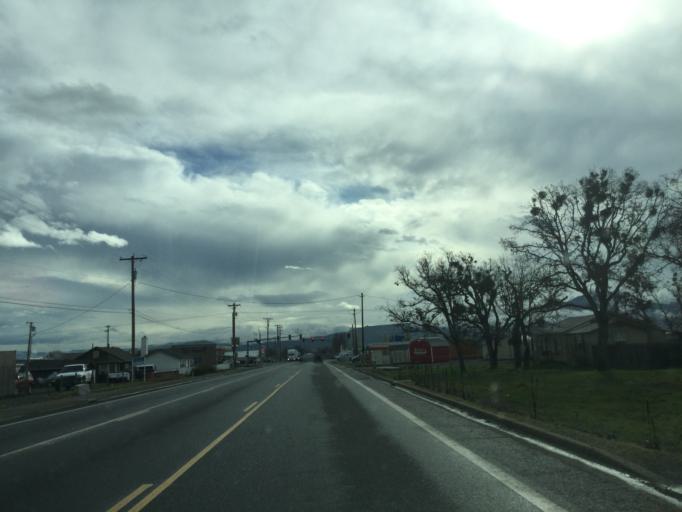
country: US
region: Oregon
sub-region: Jackson County
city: Central Point
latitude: 42.3894
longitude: -122.8879
